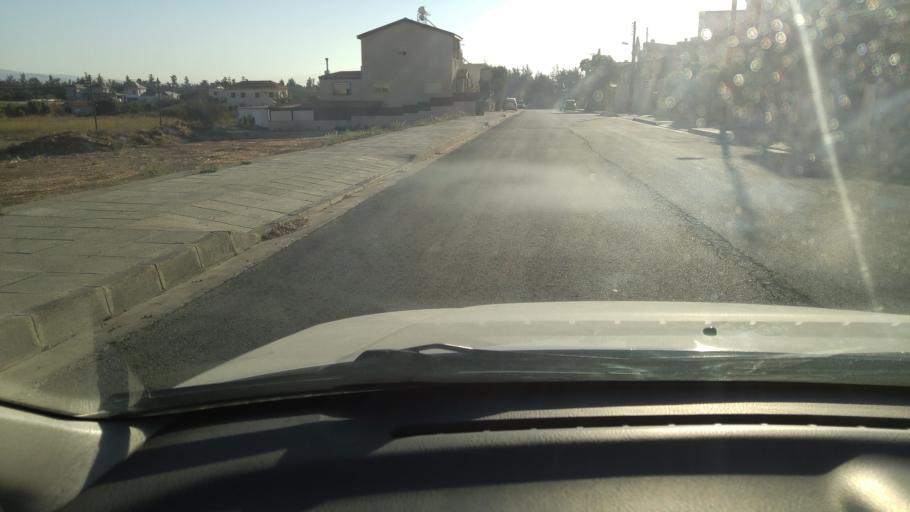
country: CY
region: Limassol
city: Ypsonas
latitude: 34.6608
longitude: 32.9673
